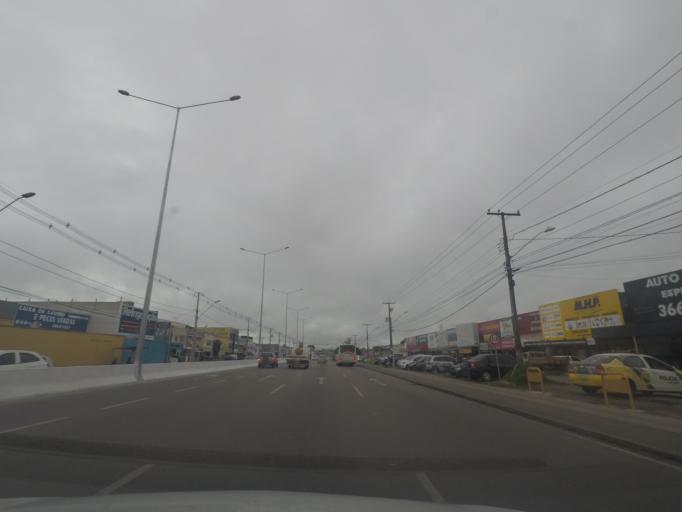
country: BR
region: Parana
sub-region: Pinhais
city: Pinhais
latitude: -25.4343
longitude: -49.1763
